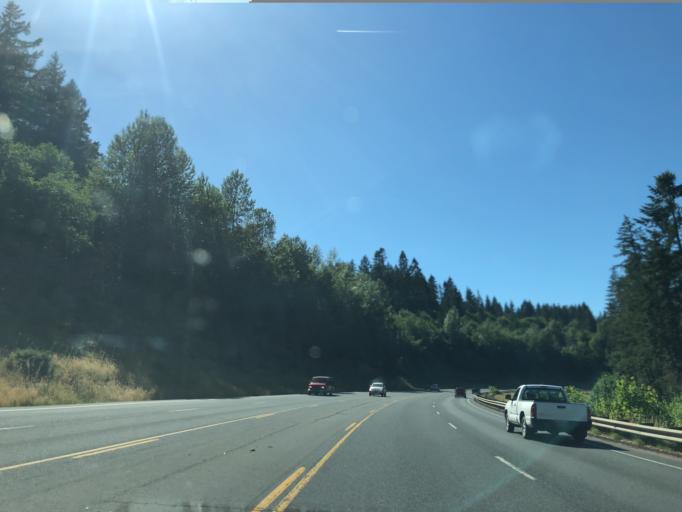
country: US
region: Oregon
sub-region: Linn County
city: Sweet Home
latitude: 44.4048
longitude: -122.7595
